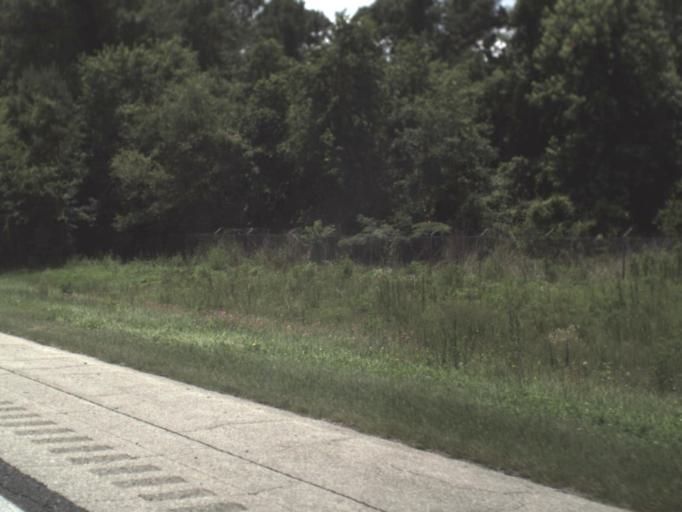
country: US
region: Florida
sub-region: Alachua County
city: Alachua
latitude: 29.6738
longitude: -82.4321
